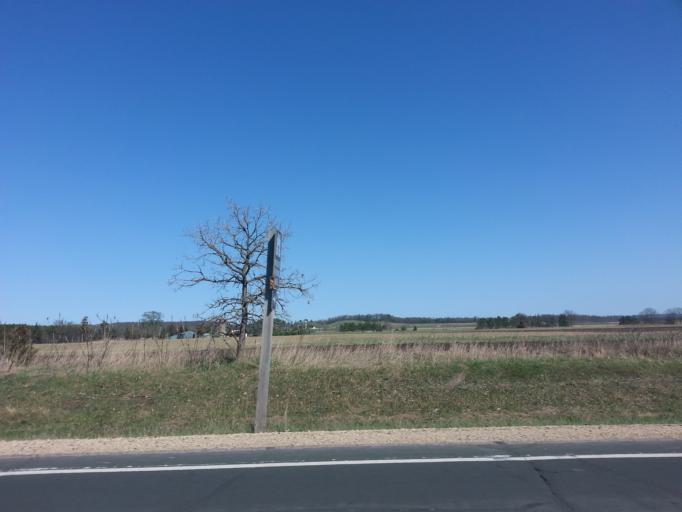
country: US
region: Wisconsin
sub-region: Pepin County
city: Durand
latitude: 44.7191
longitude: -91.9331
